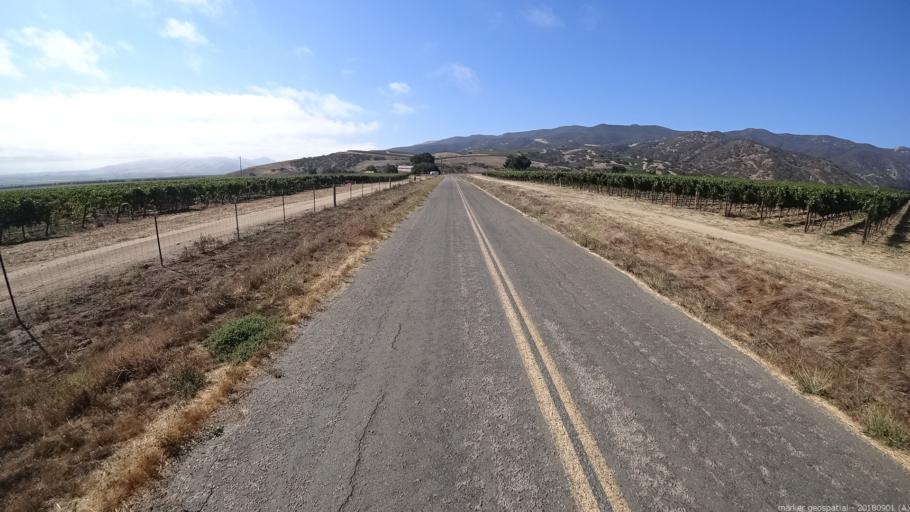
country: US
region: California
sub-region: Monterey County
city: Soledad
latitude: 36.3416
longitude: -121.3423
